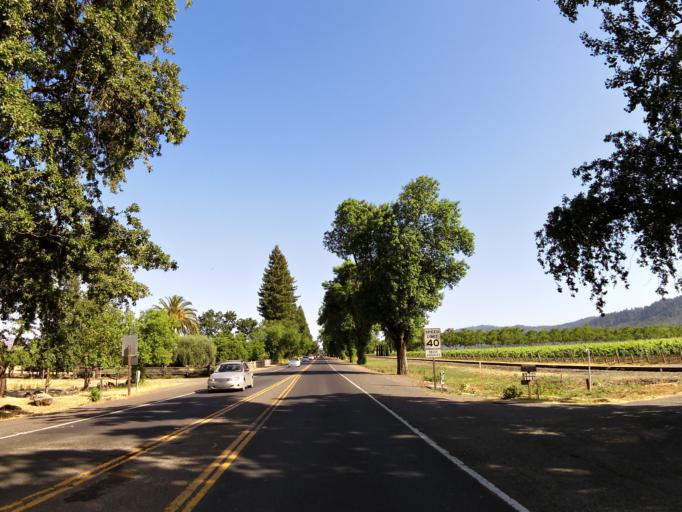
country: US
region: California
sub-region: Napa County
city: Saint Helena
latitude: 38.4647
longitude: -122.4274
